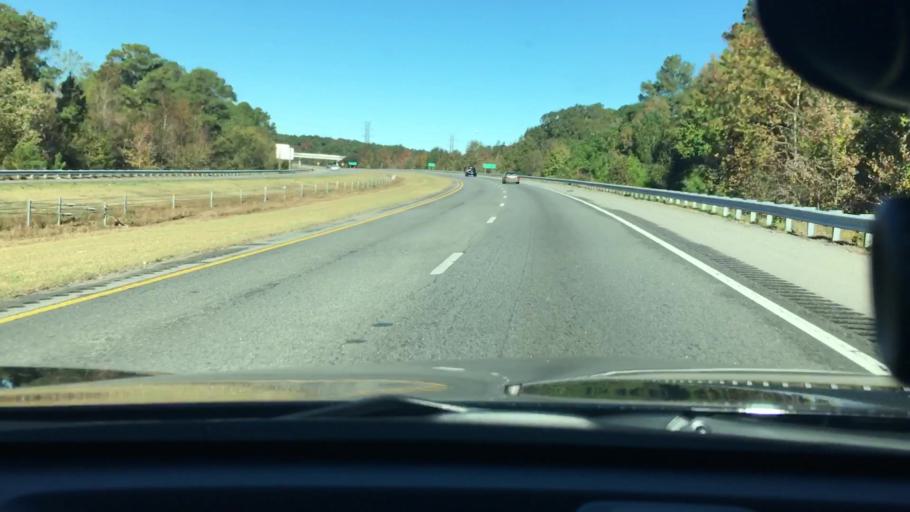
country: US
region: North Carolina
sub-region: Edgecombe County
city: Princeville
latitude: 35.8830
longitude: -77.5309
